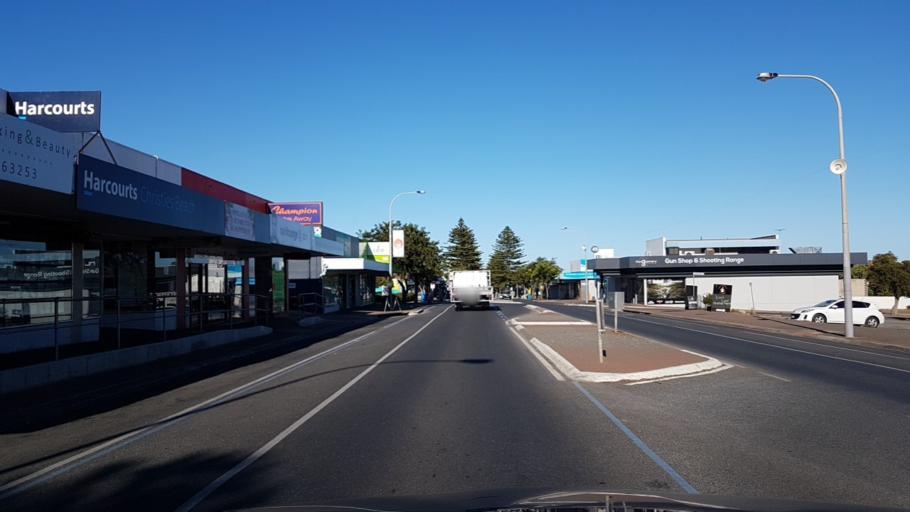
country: AU
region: South Australia
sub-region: Adelaide
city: Port Noarlunga
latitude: -35.1392
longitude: 138.4764
